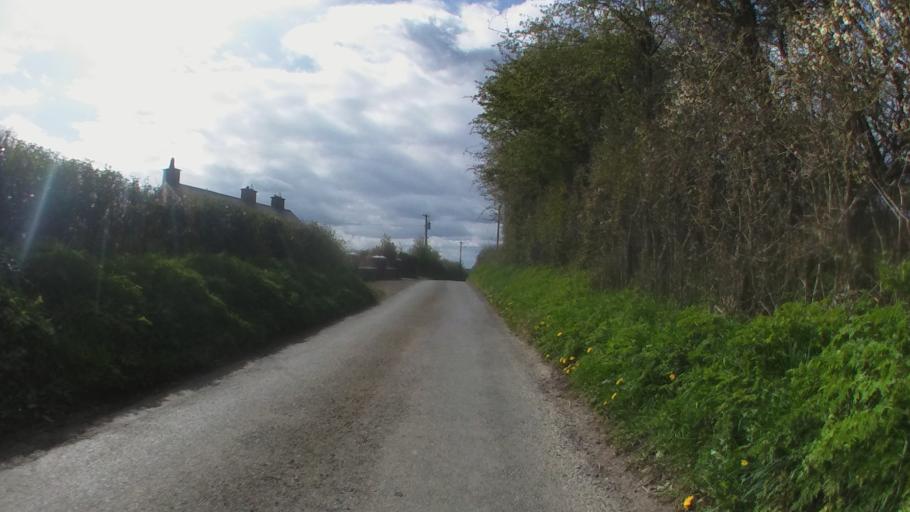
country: IE
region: Leinster
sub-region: Kilkenny
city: Kilkenny
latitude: 52.7218
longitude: -7.2295
